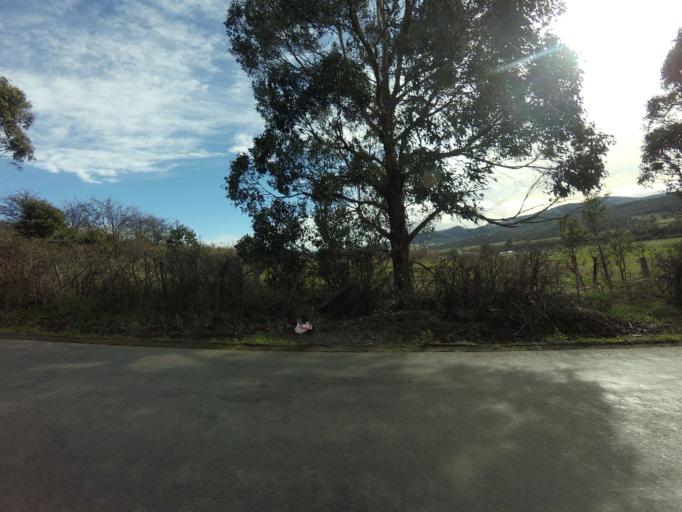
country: AU
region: Tasmania
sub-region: Derwent Valley
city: New Norfolk
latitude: -42.7748
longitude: 147.0219
